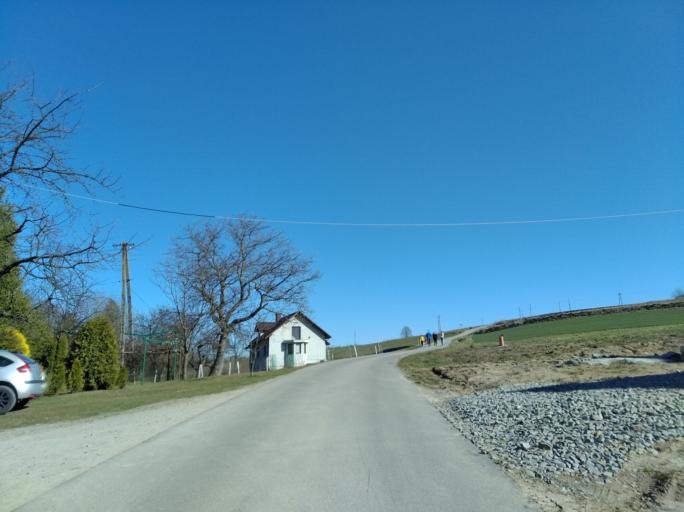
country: PL
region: Subcarpathian Voivodeship
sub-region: Powiat strzyzowski
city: Wisniowa
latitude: 49.9069
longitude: 21.6985
